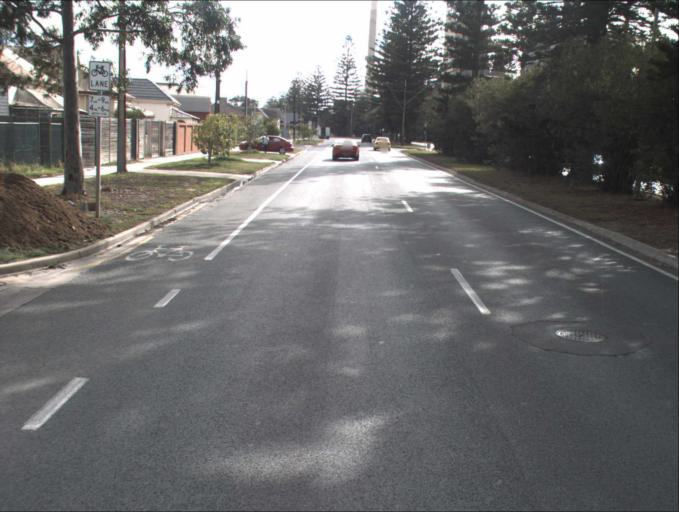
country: AU
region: South Australia
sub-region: Port Adelaide Enfield
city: Birkenhead
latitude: -34.8353
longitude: 138.5017
